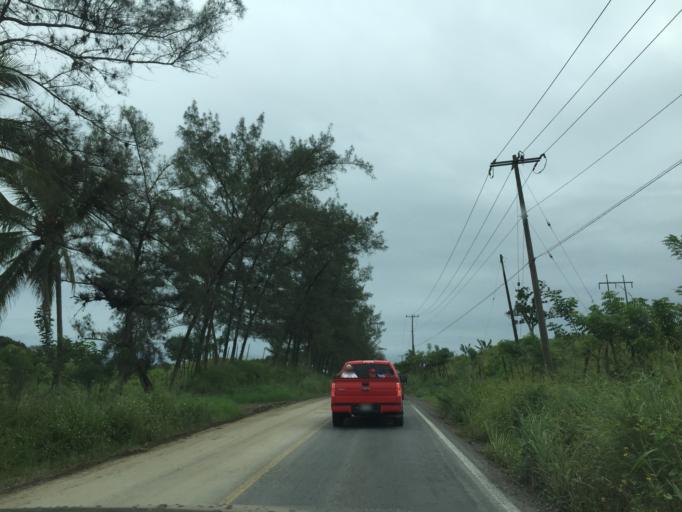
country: MX
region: Veracruz
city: Coatzintla
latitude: 20.4479
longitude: -97.4080
